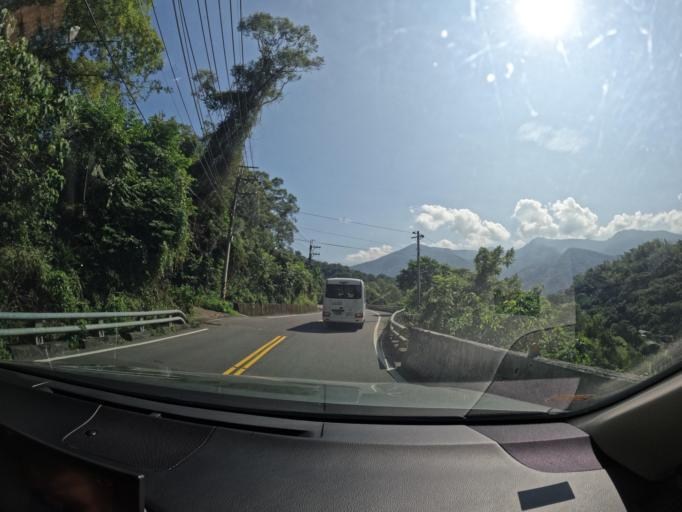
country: TW
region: Taiwan
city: Yujing
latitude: 23.0704
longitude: 120.6573
